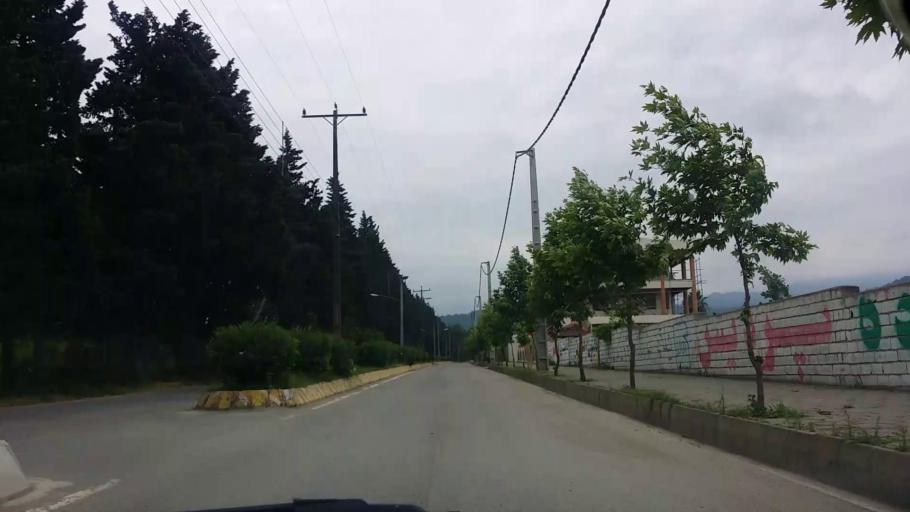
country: IR
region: Mazandaran
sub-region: Nowshahr
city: Nowshahr
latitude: 36.6366
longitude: 51.5024
